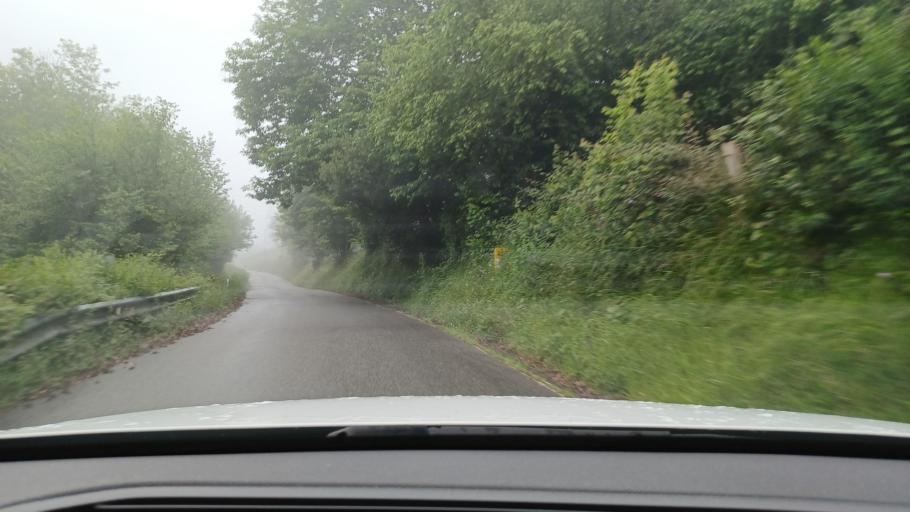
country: ES
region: Asturias
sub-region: Province of Asturias
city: Proaza
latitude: 43.2935
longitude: -5.9642
